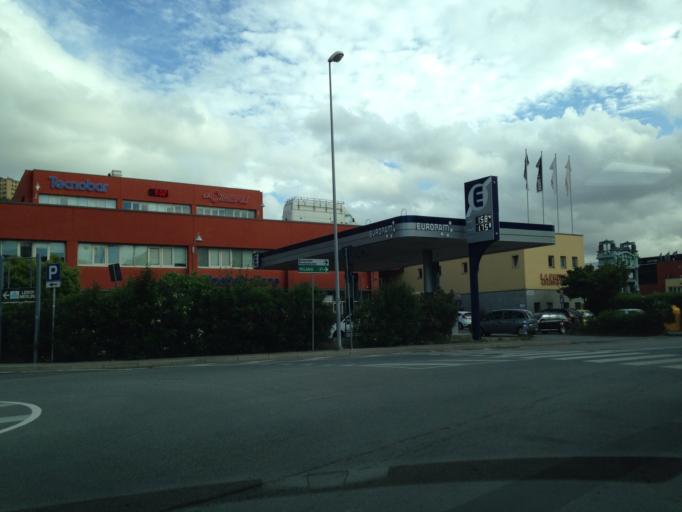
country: IT
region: Liguria
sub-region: Provincia di Genova
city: San Teodoro
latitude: 44.4207
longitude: 8.8811
